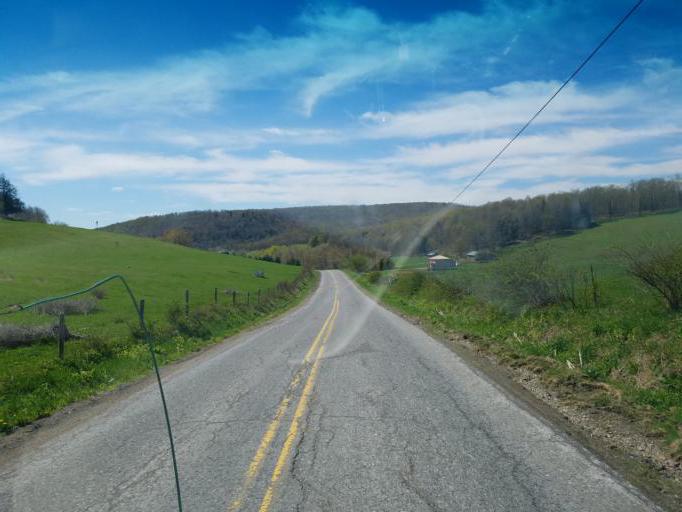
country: US
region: Pennsylvania
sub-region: Potter County
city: Galeton
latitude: 41.8852
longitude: -77.7374
